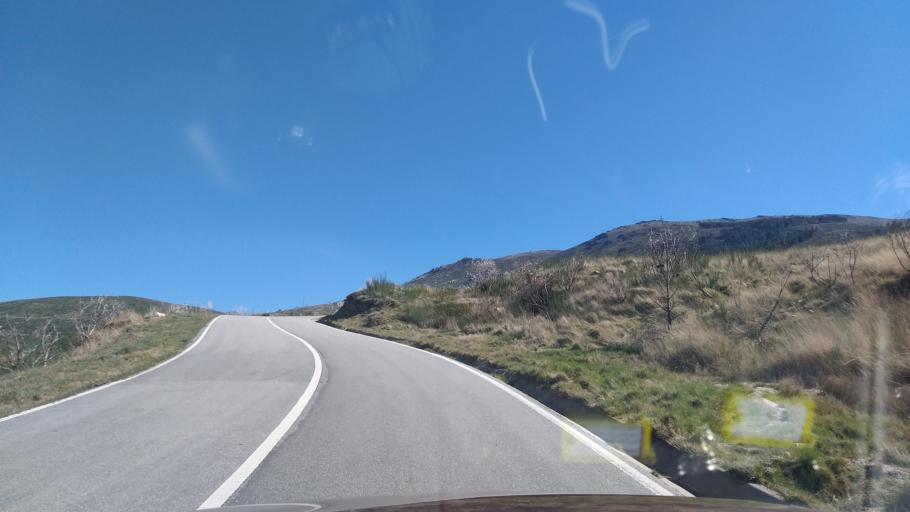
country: PT
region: Guarda
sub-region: Manteigas
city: Manteigas
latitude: 40.4878
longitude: -7.5646
